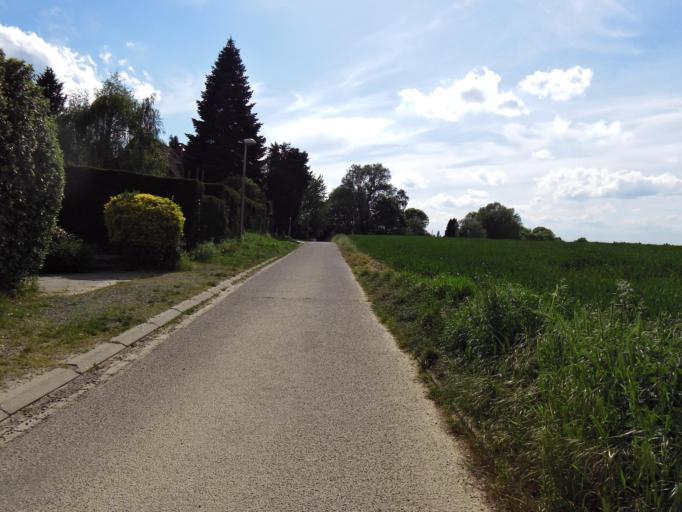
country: BE
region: Flanders
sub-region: Provincie Vlaams-Brabant
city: Wezembeek-Oppem
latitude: 50.8471
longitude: 4.4984
